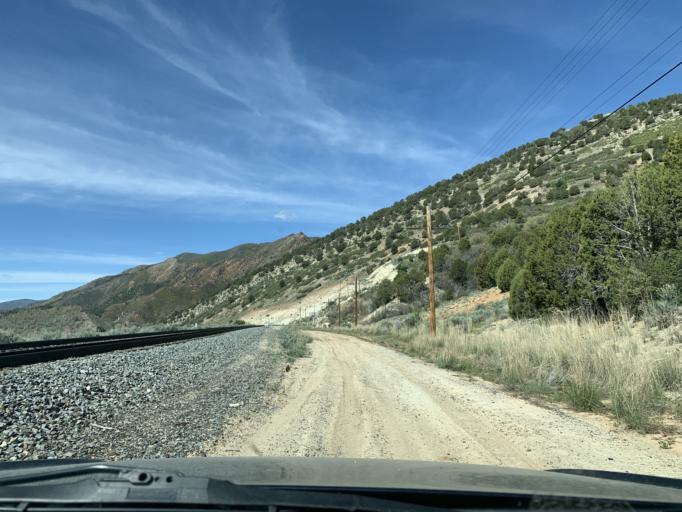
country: US
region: Utah
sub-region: Utah County
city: Mapleton
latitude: 39.9987
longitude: -111.4862
